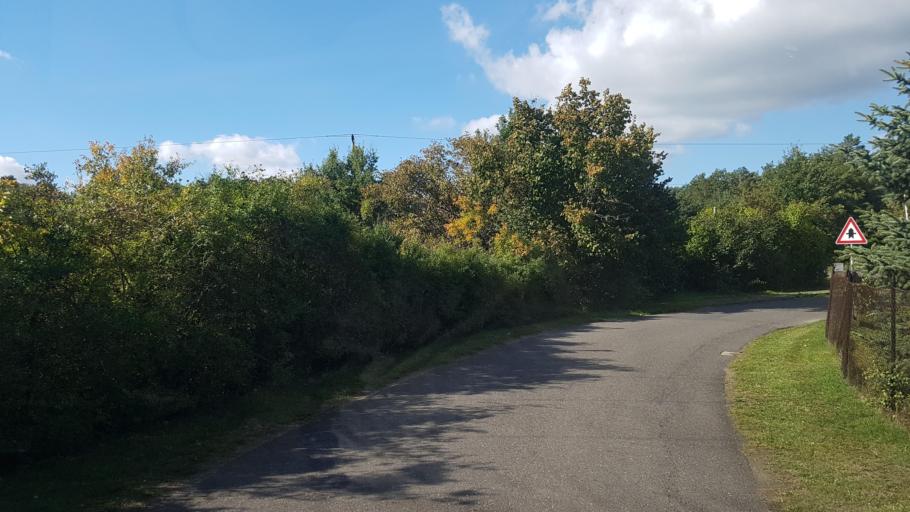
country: DE
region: Brandenburg
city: Drehnow
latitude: 51.8065
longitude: 14.3779
